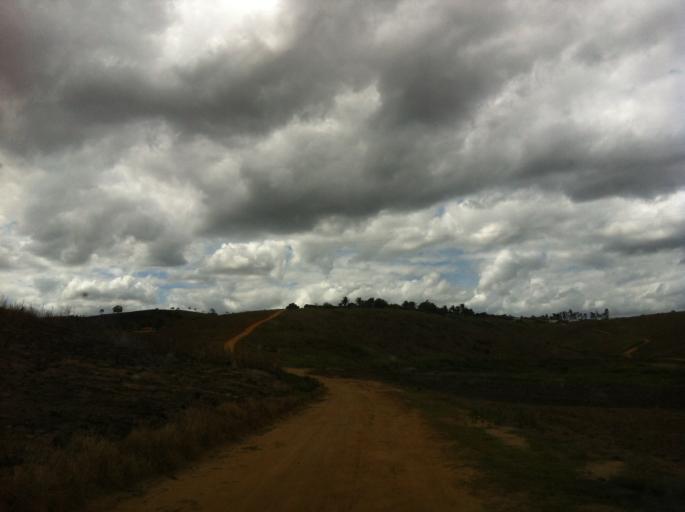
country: BR
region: Alagoas
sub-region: Ibateguara
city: Ibateguara
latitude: -8.9561
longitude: -35.9523
